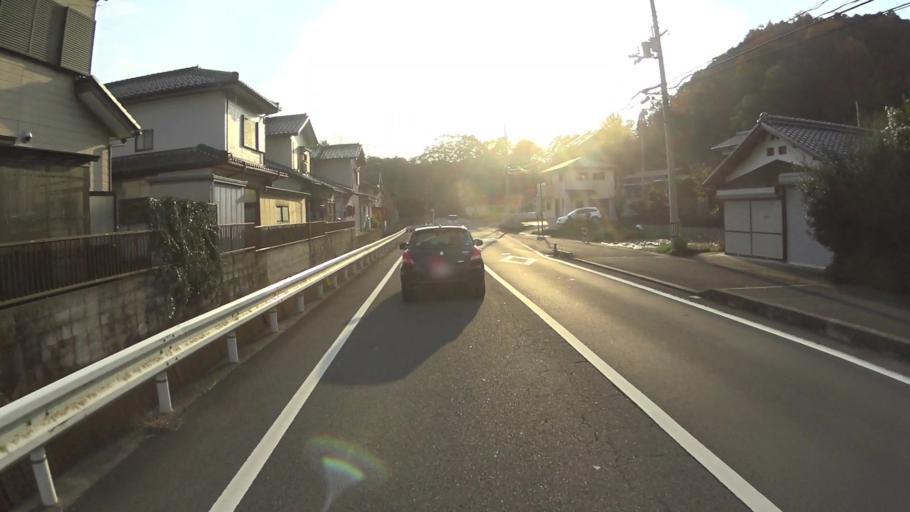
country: JP
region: Kyoto
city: Maizuru
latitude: 35.4863
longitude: 135.4352
